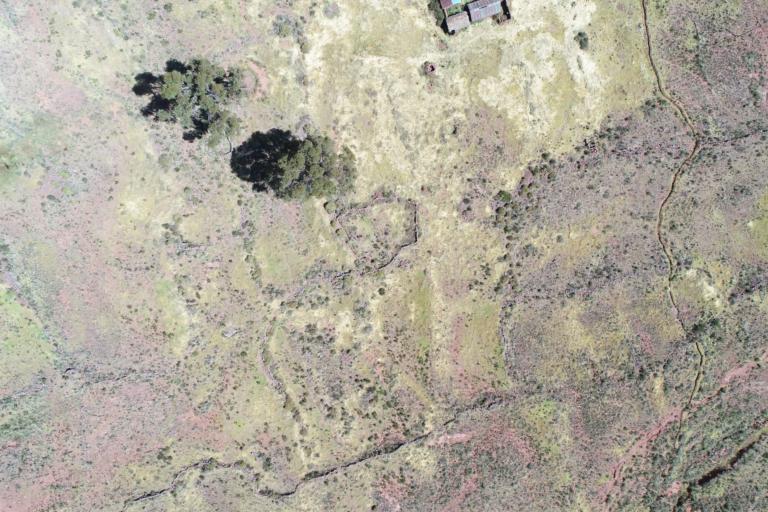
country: BO
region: La Paz
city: Tiahuanaco
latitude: -16.6074
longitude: -68.7688
